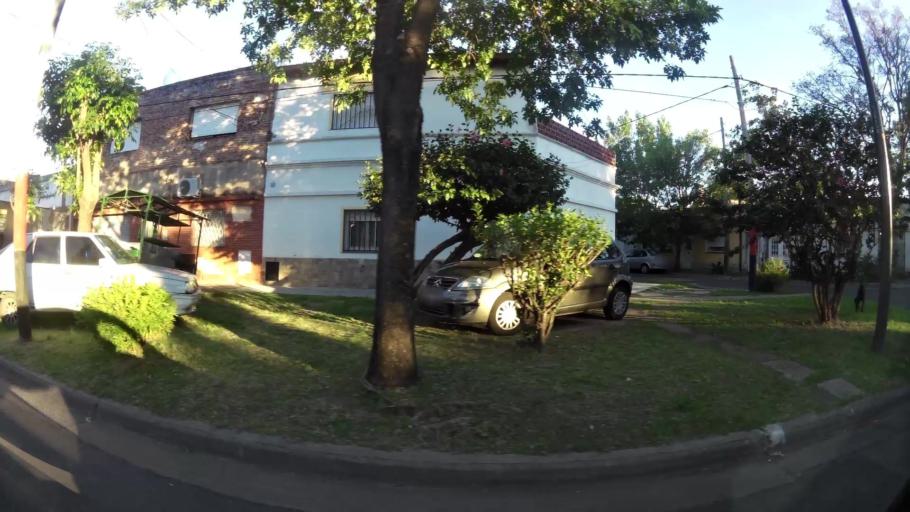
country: AR
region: Santa Fe
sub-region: Departamento de Rosario
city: Rosario
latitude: -32.9683
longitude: -60.6690
